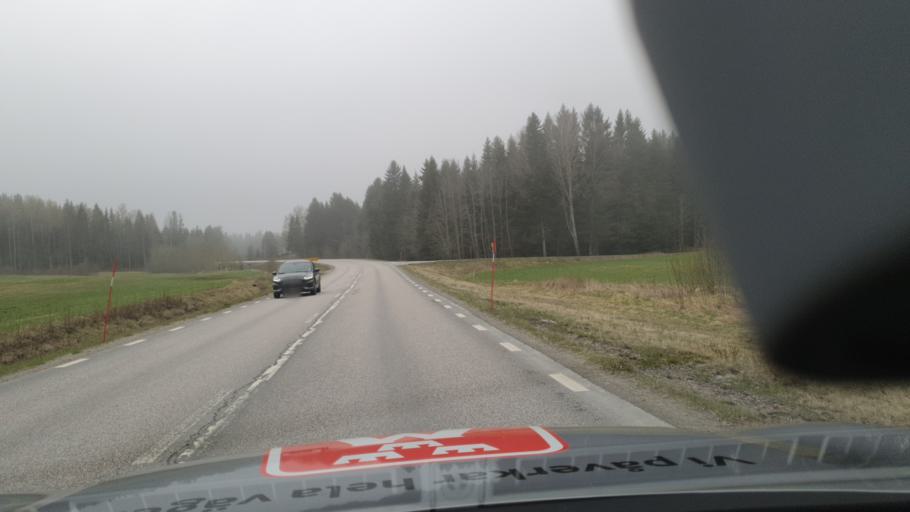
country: SE
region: Vaesternorrland
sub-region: OErnskoeldsviks Kommun
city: Ornskoldsvik
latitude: 63.3374
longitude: 18.7975
